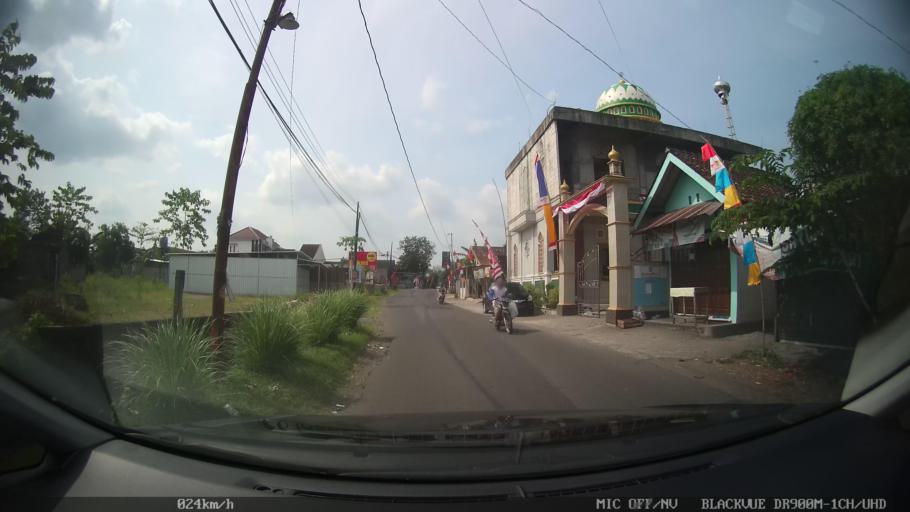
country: ID
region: Daerah Istimewa Yogyakarta
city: Depok
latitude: -7.7923
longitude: 110.4461
